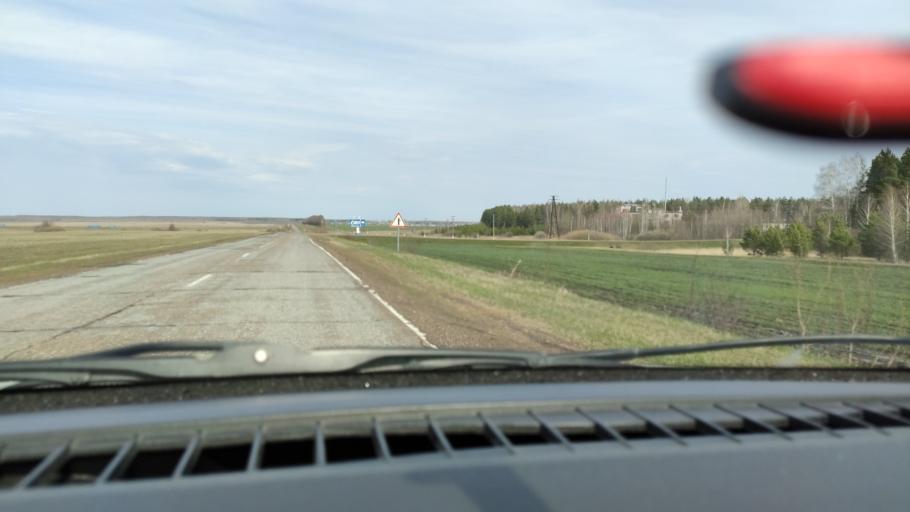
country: RU
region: Bashkortostan
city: Dyurtyuli
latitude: 55.2838
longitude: 55.0619
